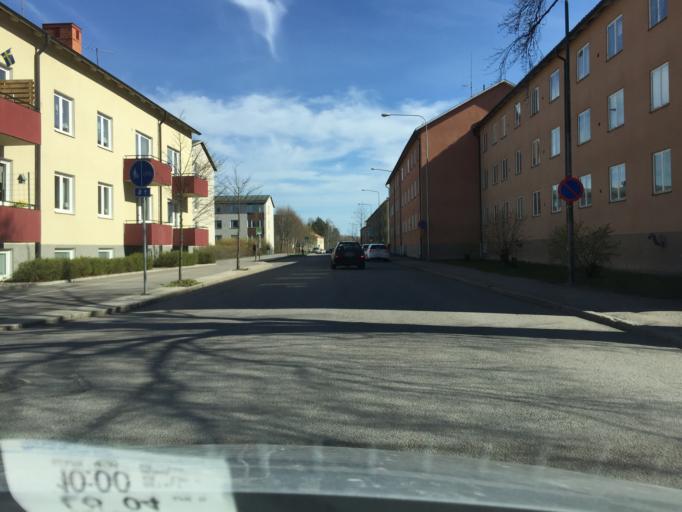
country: SE
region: Soedermanland
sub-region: Katrineholms Kommun
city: Katrineholm
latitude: 58.9954
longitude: 16.2152
